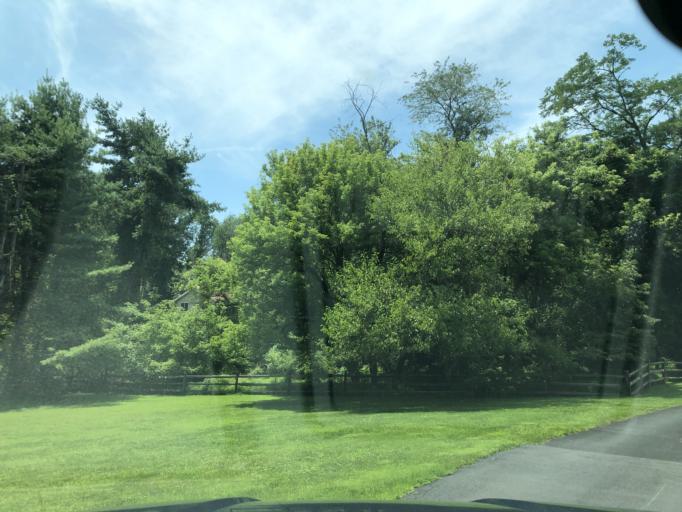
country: US
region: Maryland
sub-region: Baltimore County
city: Garrison
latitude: 39.4579
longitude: -76.7229
